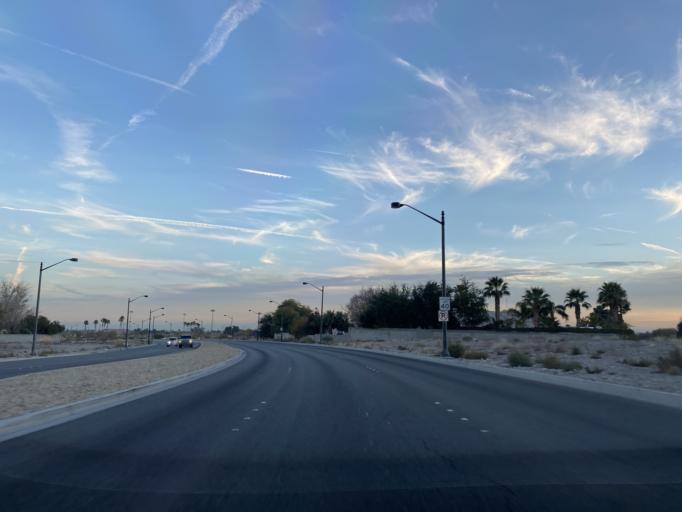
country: US
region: Nevada
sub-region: Clark County
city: Summerlin South
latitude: 36.2762
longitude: -115.2877
